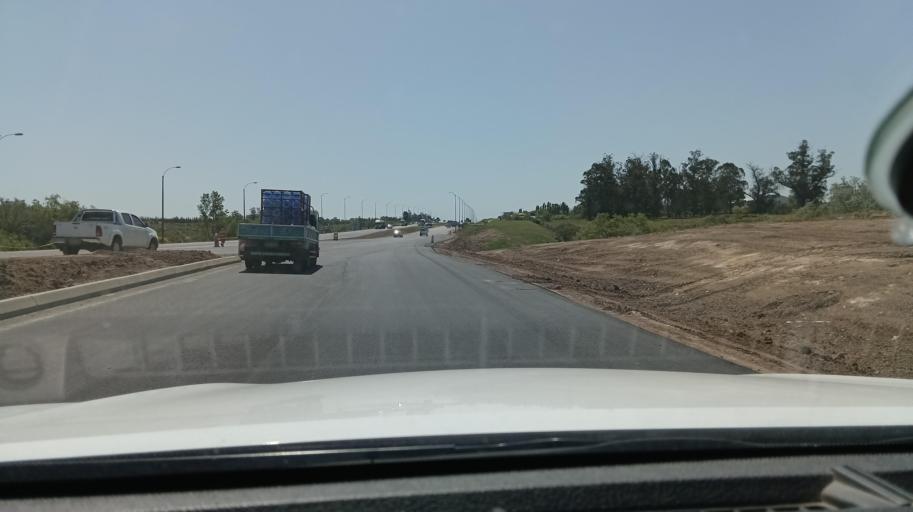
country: UY
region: Canelones
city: La Paz
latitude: -34.8138
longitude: -56.2588
